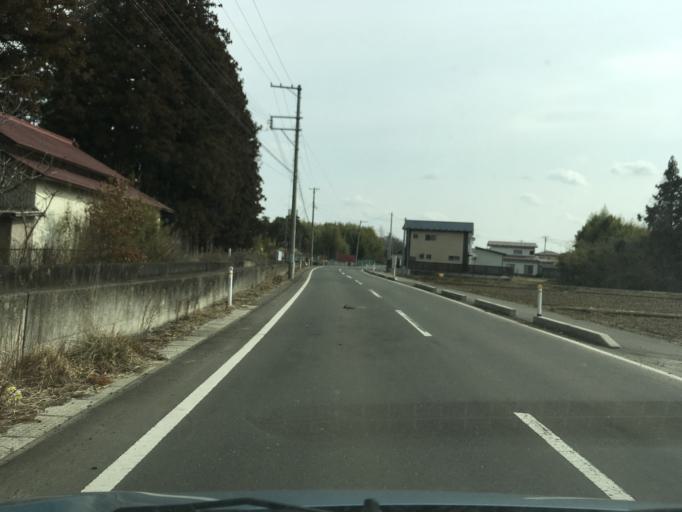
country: JP
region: Miyagi
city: Wakuya
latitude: 38.7207
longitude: 141.2418
